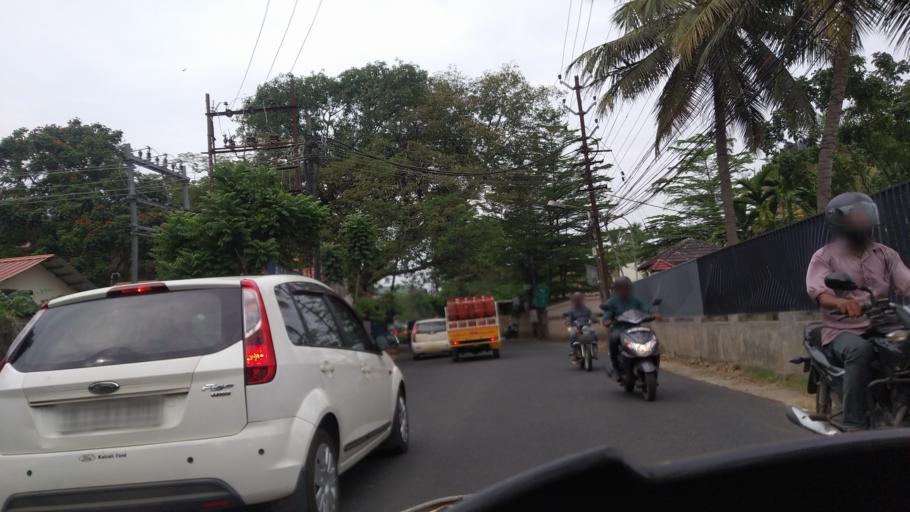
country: IN
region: Kerala
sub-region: Ernakulam
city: Cochin
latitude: 9.9380
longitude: 76.2969
